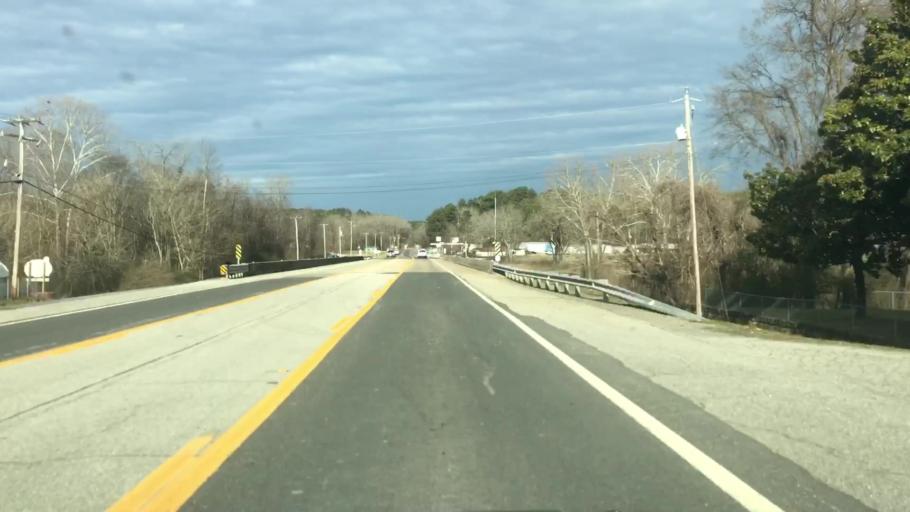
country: US
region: Arkansas
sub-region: Montgomery County
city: Mount Ida
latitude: 34.5598
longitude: -93.6353
